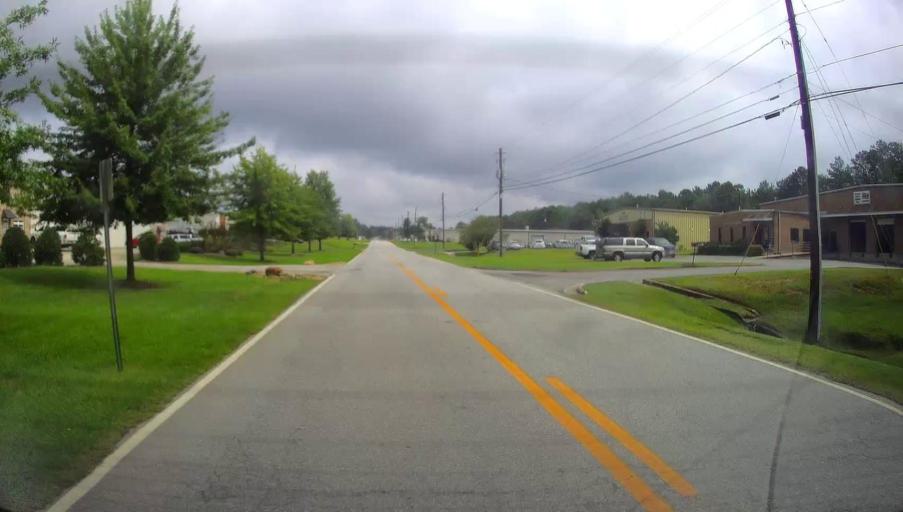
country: US
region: Georgia
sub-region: Bibb County
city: West Point
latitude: 32.8250
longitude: -83.7293
